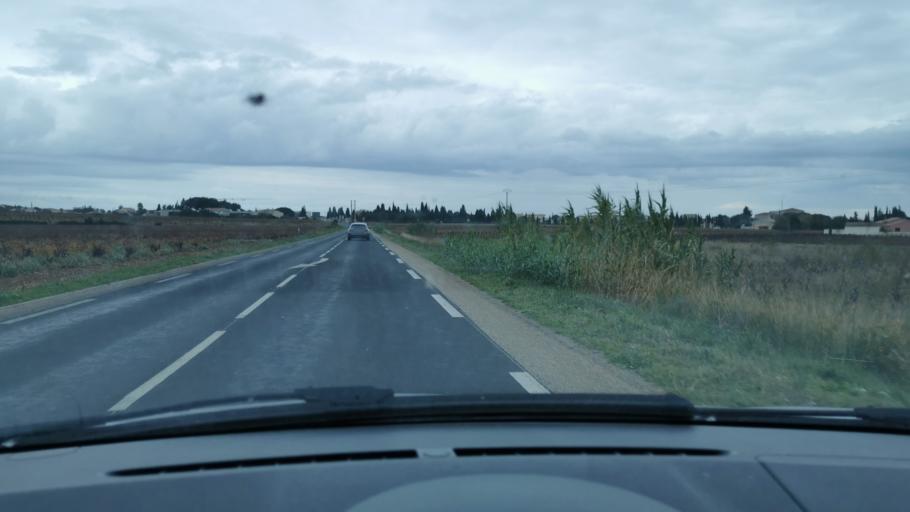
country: FR
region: Languedoc-Roussillon
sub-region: Departement de l'Herault
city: Frontignan
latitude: 43.4477
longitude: 3.7355
